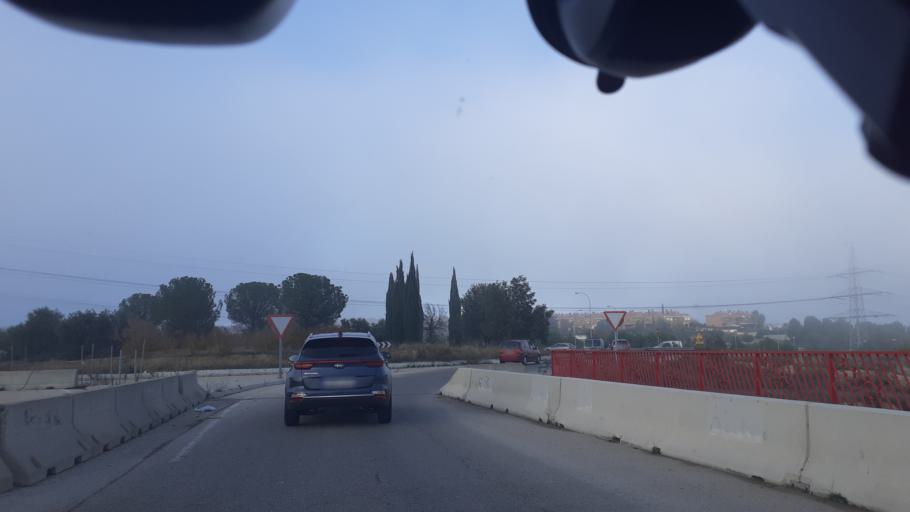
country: ES
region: Madrid
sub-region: Provincia de Madrid
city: Coslada
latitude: 40.4109
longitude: -3.5514
